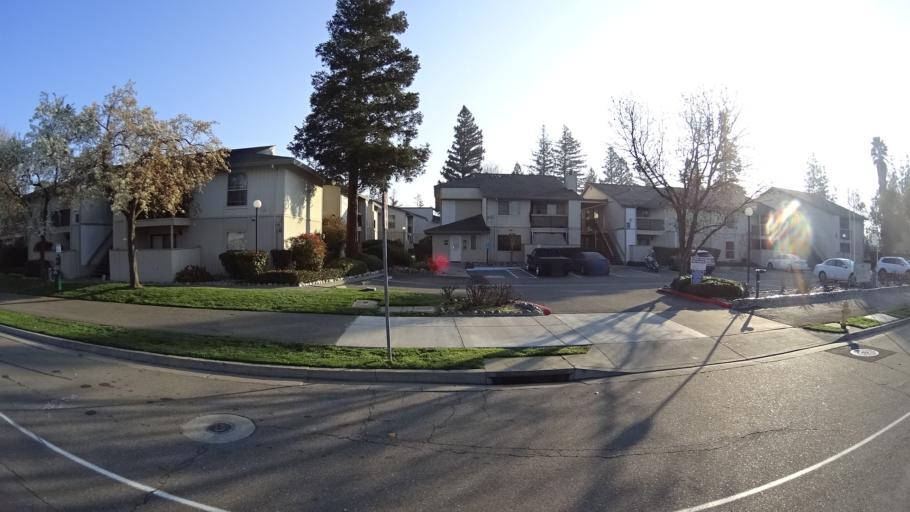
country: US
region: California
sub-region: Yolo County
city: Davis
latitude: 38.5528
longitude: -121.7875
